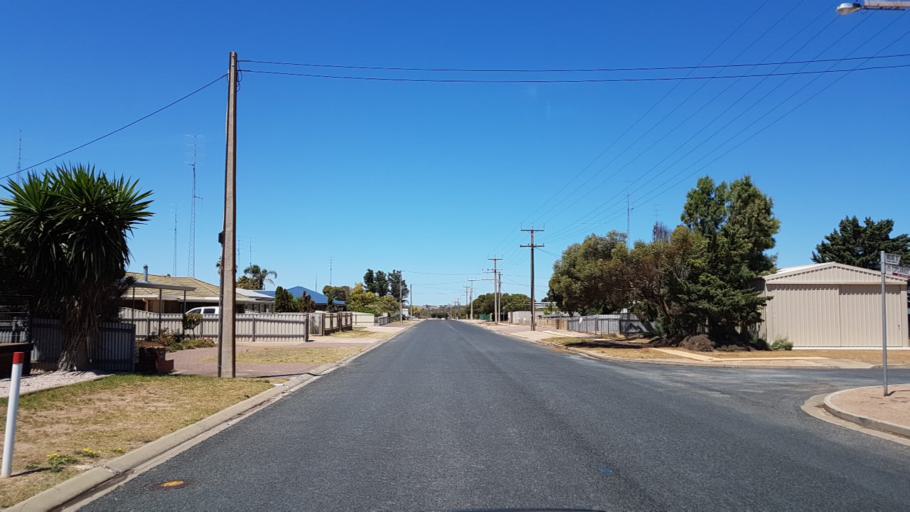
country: AU
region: South Australia
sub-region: Copper Coast
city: Wallaroo
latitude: -33.9027
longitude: 137.6317
